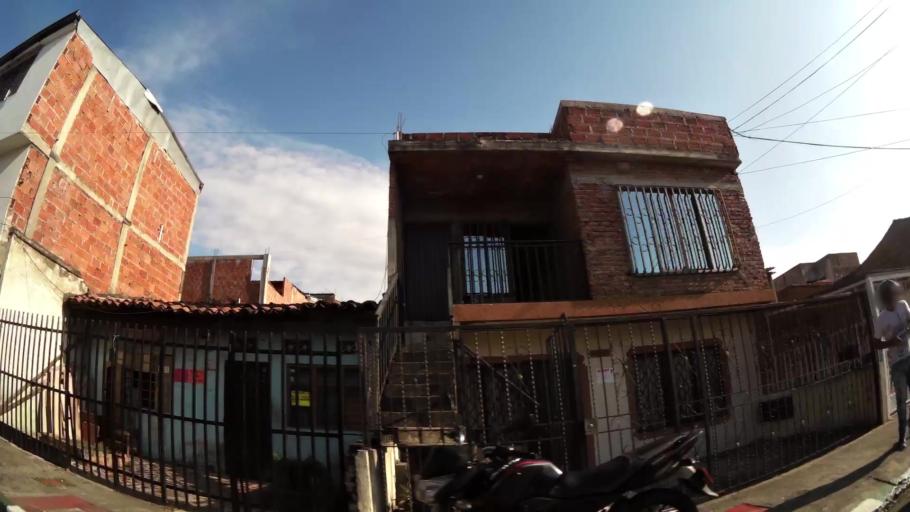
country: CO
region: Valle del Cauca
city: Cali
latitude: 3.4274
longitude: -76.5162
